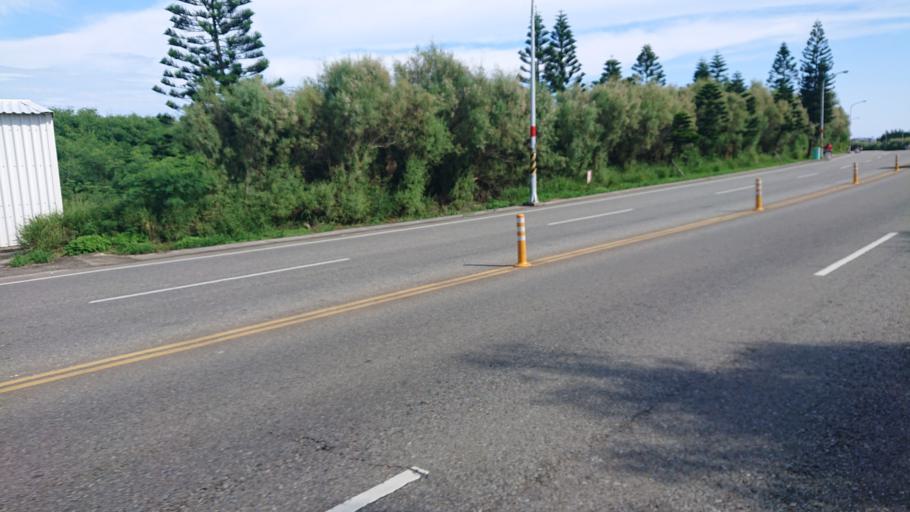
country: TW
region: Taiwan
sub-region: Penghu
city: Ma-kung
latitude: 23.5460
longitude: 119.6071
